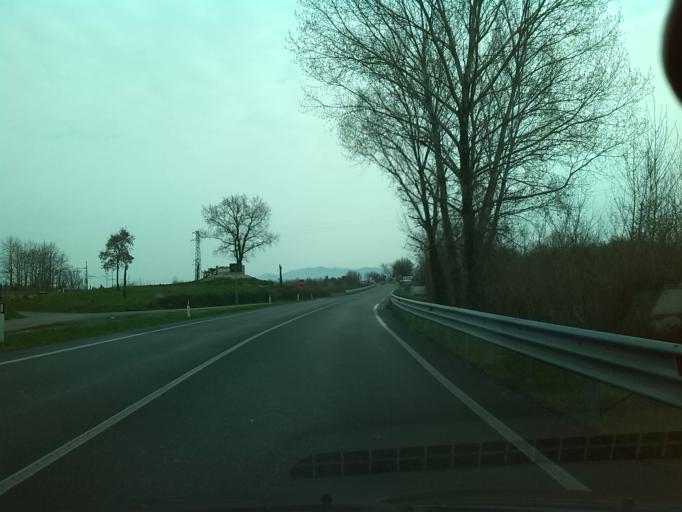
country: IT
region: Friuli Venezia Giulia
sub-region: Provincia di Gorizia
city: Moraro
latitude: 45.9441
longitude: 13.4926
